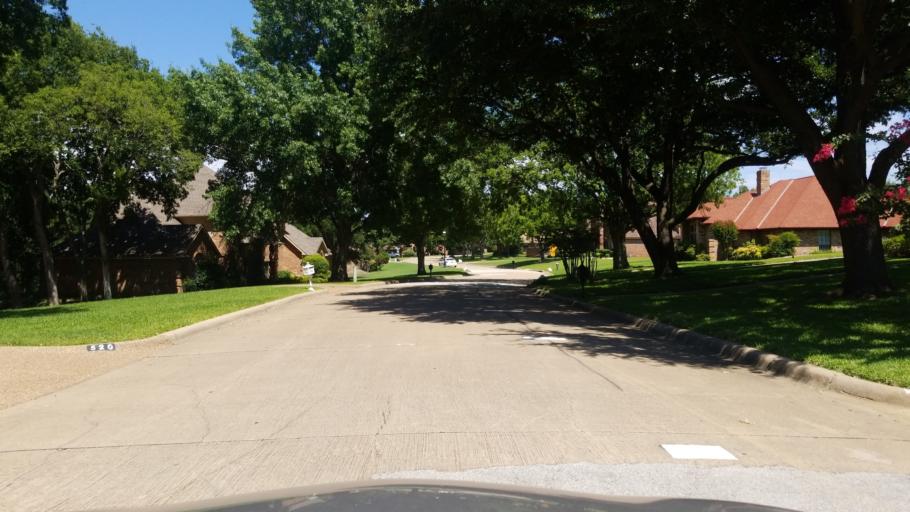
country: US
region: Texas
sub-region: Dallas County
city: Grand Prairie
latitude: 32.6872
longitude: -97.0007
